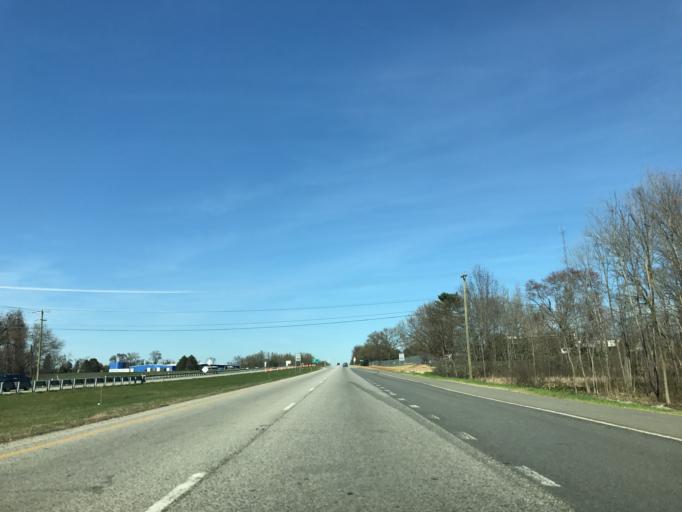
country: US
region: Maryland
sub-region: Queen Anne's County
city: Centreville
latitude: 39.0298
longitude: -76.0241
